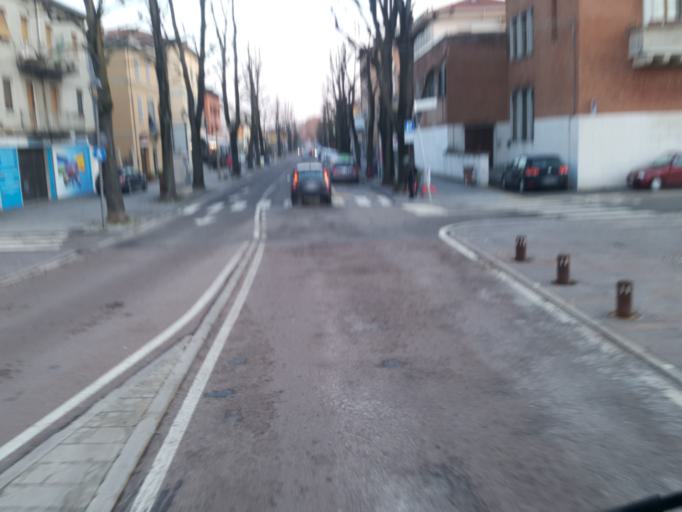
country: IT
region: Emilia-Romagna
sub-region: Provincia di Parma
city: Sorbolo
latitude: 44.8463
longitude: 10.4485
